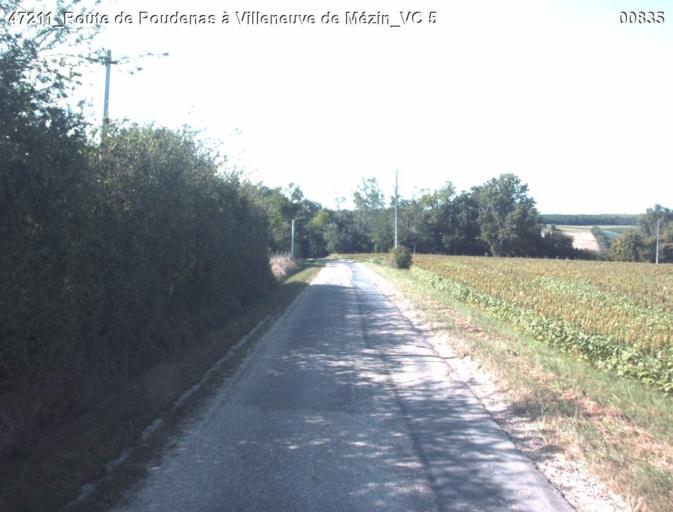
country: FR
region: Aquitaine
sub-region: Departement du Lot-et-Garonne
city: Mezin
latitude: 44.0412
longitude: 0.2181
